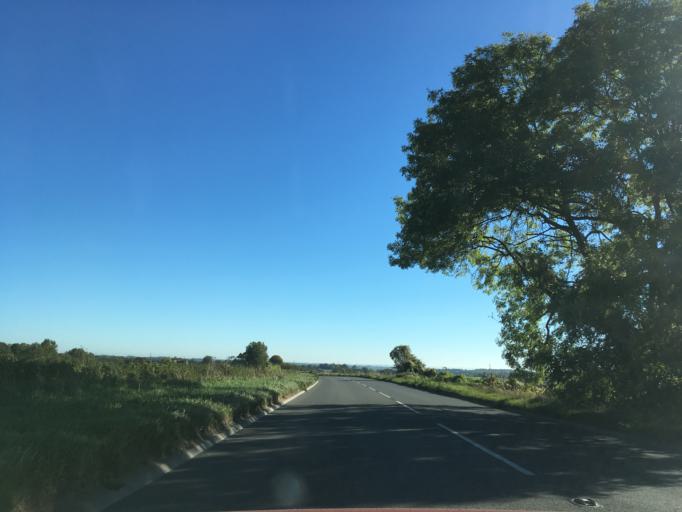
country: GB
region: England
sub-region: South Gloucestershire
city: Marshfield
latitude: 51.4648
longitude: -2.2905
